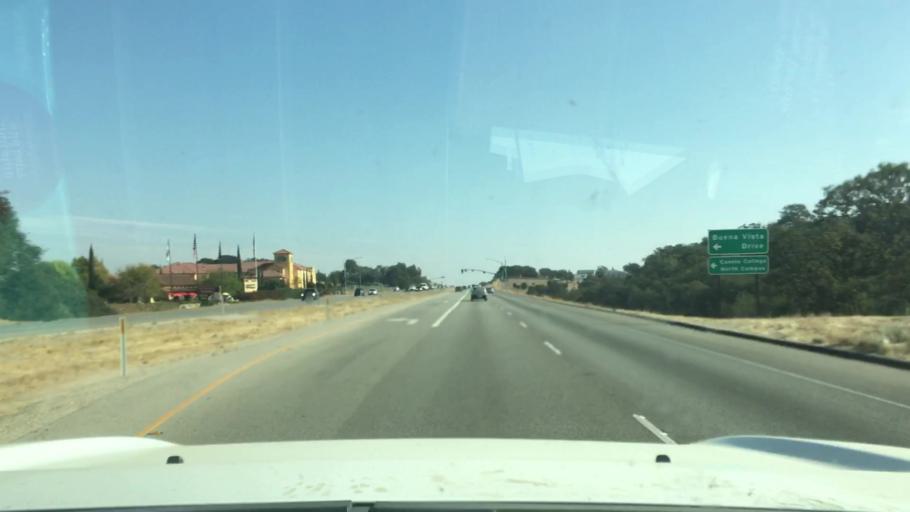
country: US
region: California
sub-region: San Luis Obispo County
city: Paso Robles
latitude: 35.6445
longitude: -120.6752
